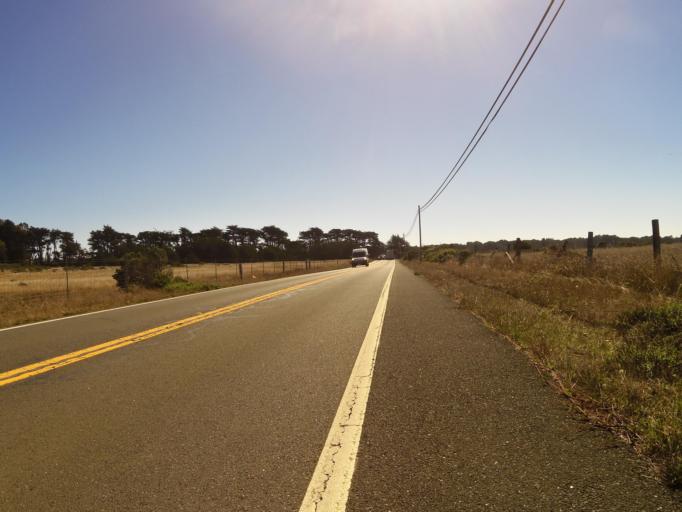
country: US
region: California
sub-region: Mendocino County
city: Boonville
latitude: 38.9860
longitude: -123.6854
